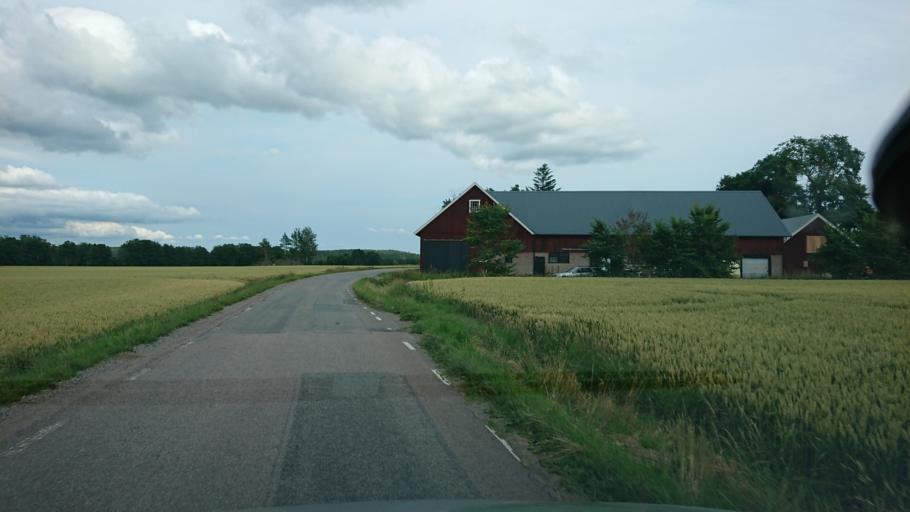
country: SE
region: Uppsala
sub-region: Osthammars Kommun
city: Bjorklinge
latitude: 59.9901
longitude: 17.5380
